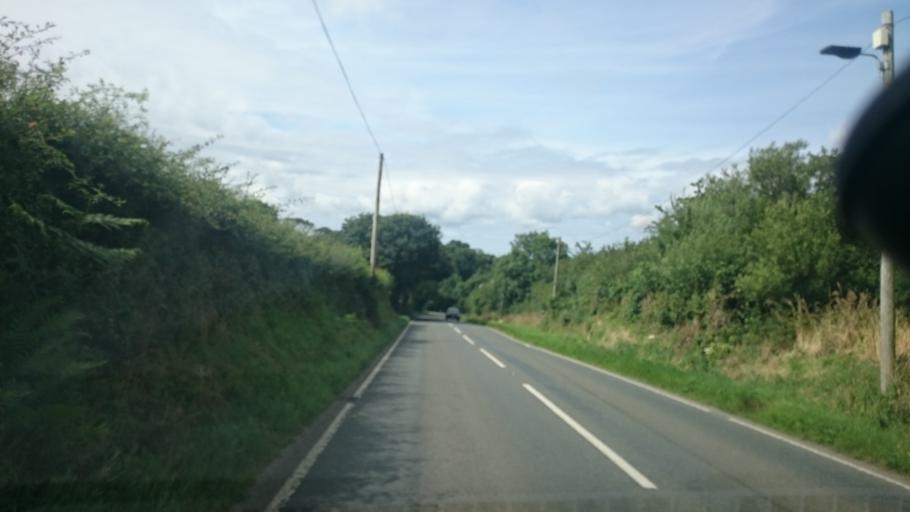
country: GB
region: Wales
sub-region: Pembrokeshire
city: Freystrop
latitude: 51.7663
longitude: -4.9615
